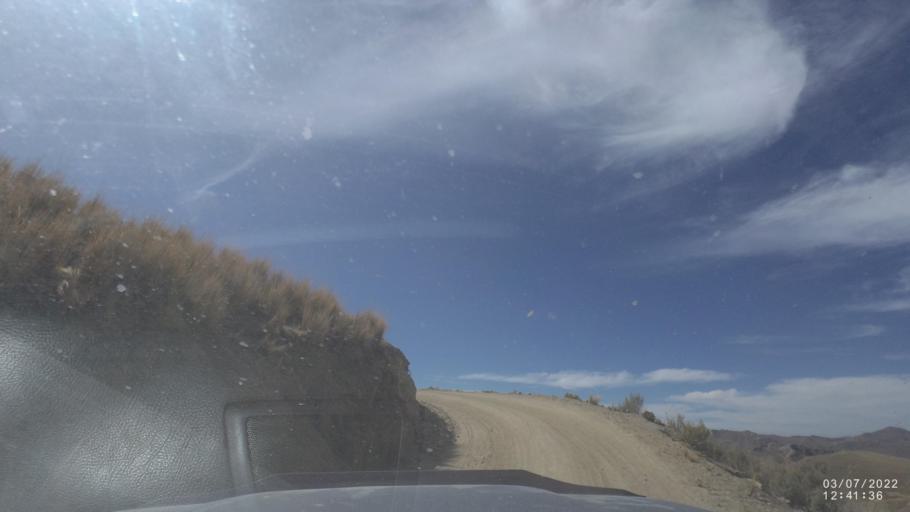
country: BO
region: Cochabamba
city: Irpa Irpa
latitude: -17.7858
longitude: -66.6247
